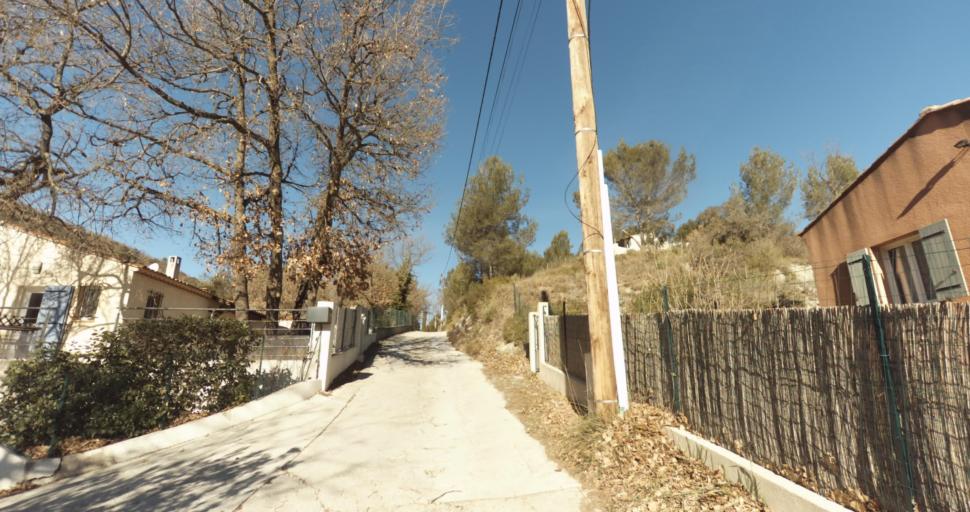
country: FR
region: Provence-Alpes-Cote d'Azur
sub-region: Departement des Bouches-du-Rhone
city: Peypin
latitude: 43.3765
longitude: 5.5681
